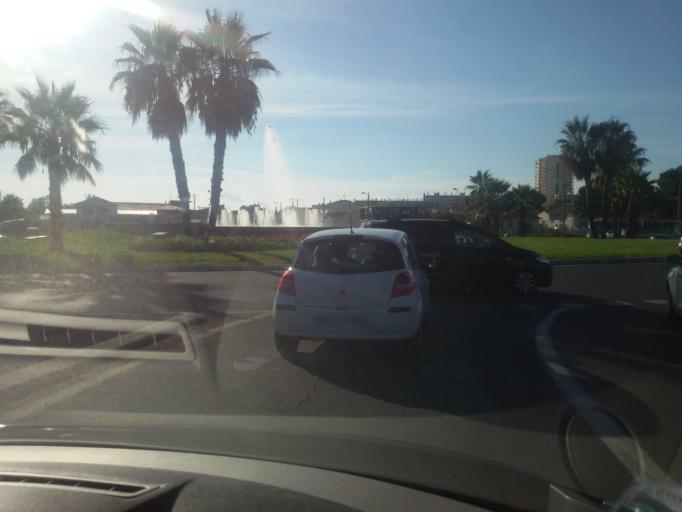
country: FR
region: Languedoc-Roussillon
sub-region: Departement de l'Herault
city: Lattes
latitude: 43.5891
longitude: 3.8909
